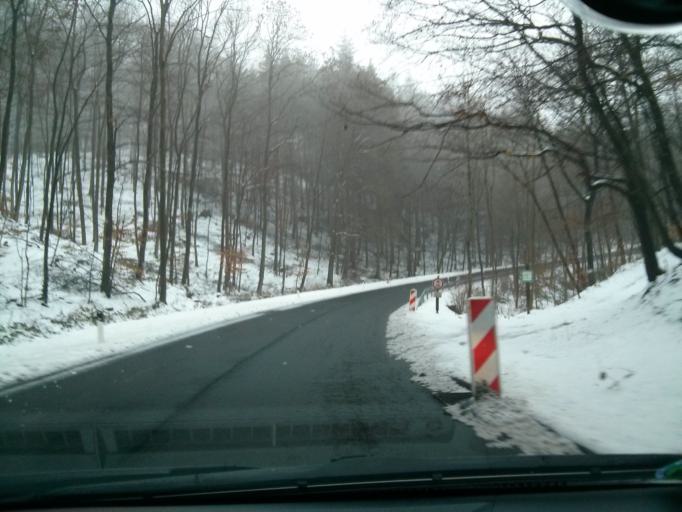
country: DE
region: Rheinland-Pfalz
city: Berg
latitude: 50.5780
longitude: 6.9357
